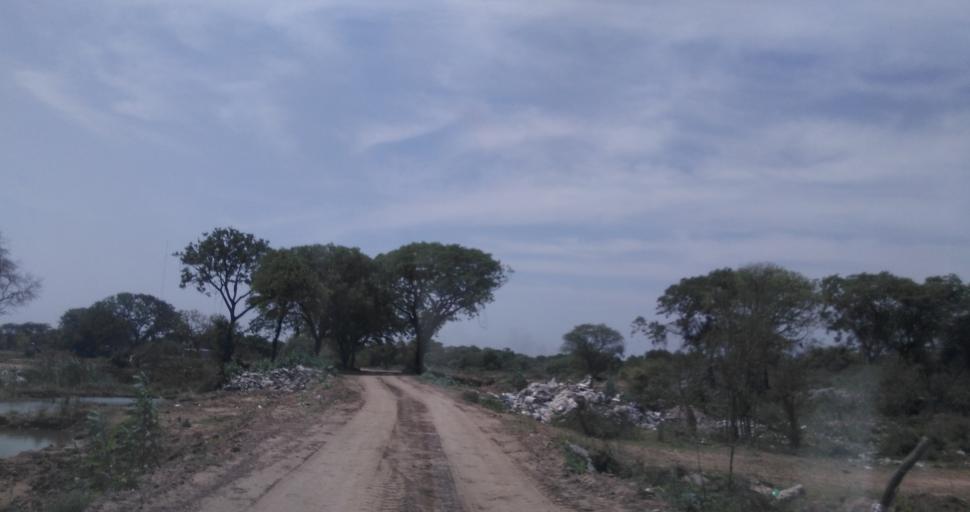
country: AR
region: Chaco
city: Fontana
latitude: -27.4193
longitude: -59.0138
